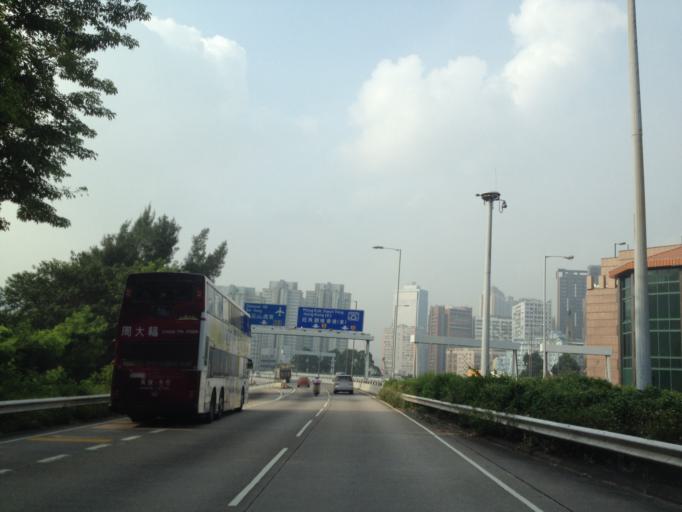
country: HK
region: Wong Tai Sin
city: Wong Tai Sin
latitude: 22.3410
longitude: 114.2042
